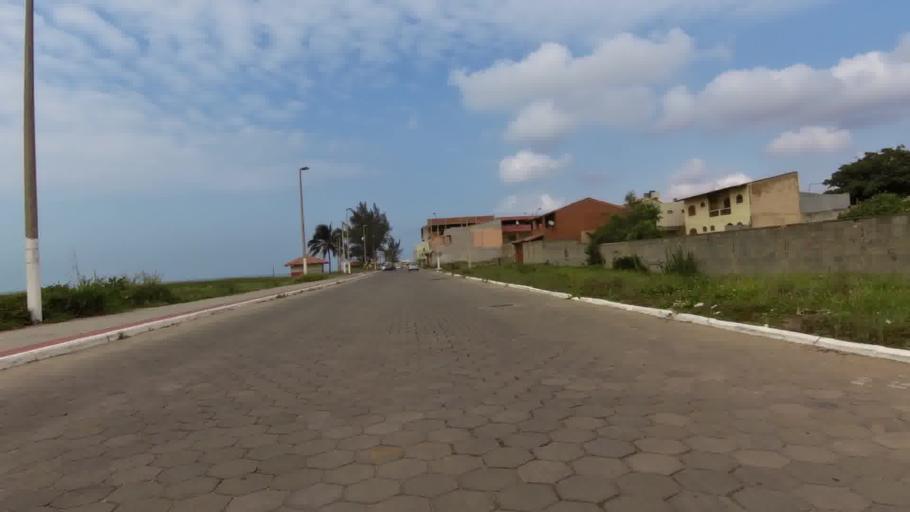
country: BR
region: Espirito Santo
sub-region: Marataizes
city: Marataizes
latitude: -21.0254
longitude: -40.8118
